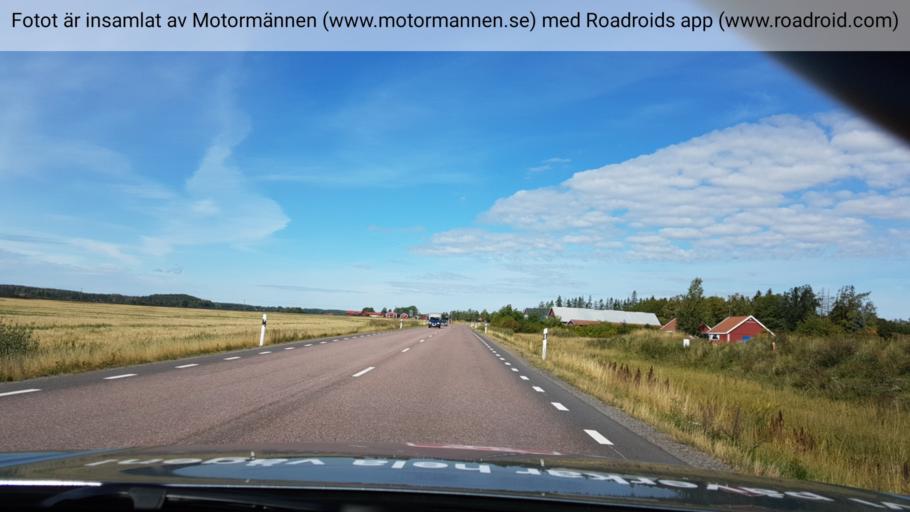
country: SE
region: Uppsala
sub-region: Osthammars Kommun
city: Bjorklinge
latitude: 59.9166
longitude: 17.5151
